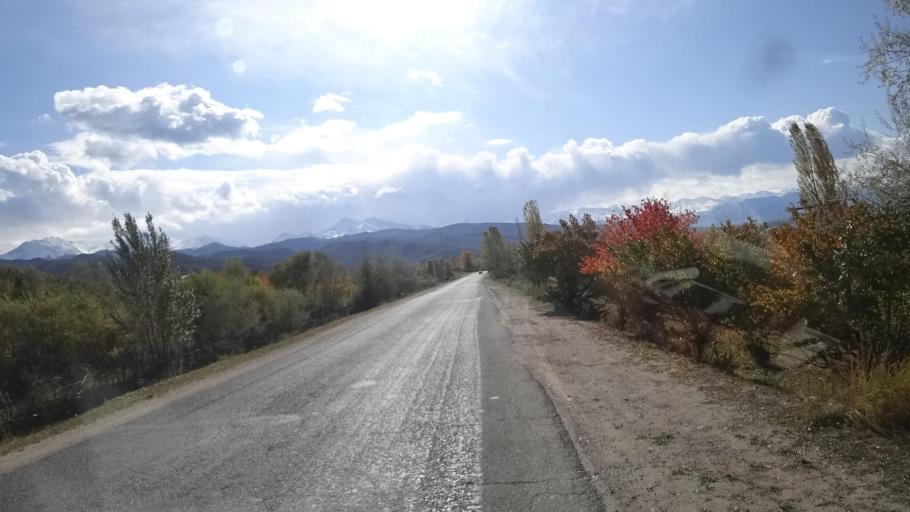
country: KG
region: Ysyk-Koel
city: Pokrovka
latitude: 42.2292
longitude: 77.7149
